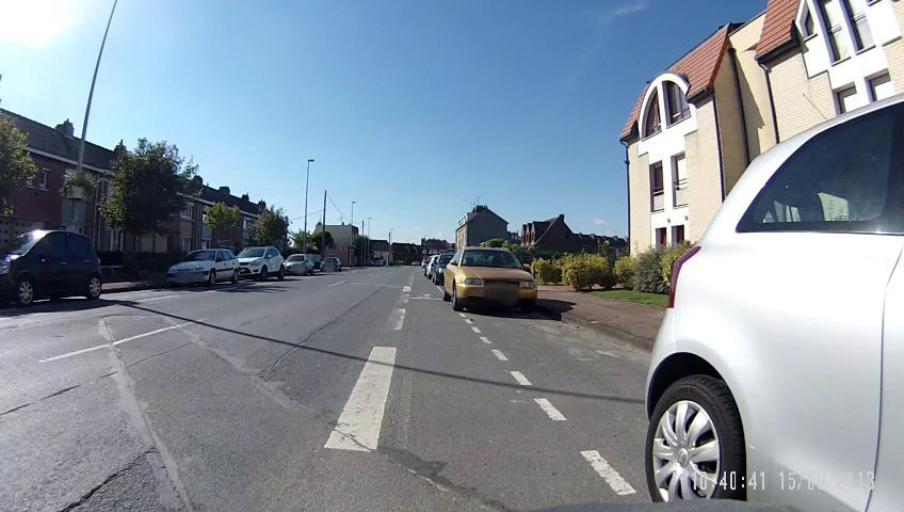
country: FR
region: Nord-Pas-de-Calais
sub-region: Departement du Nord
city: Leffrinckoucke
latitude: 51.0552
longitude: 2.4361
